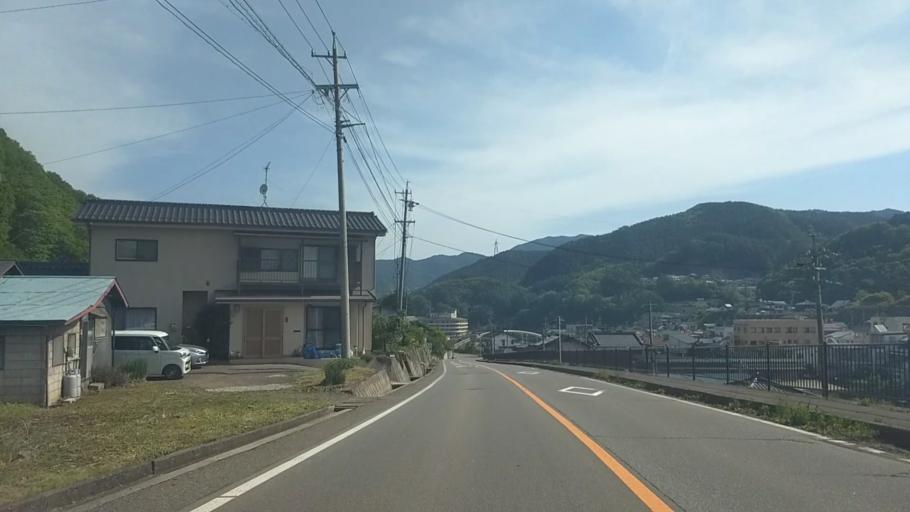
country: JP
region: Nagano
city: Saku
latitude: 36.0878
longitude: 138.4805
